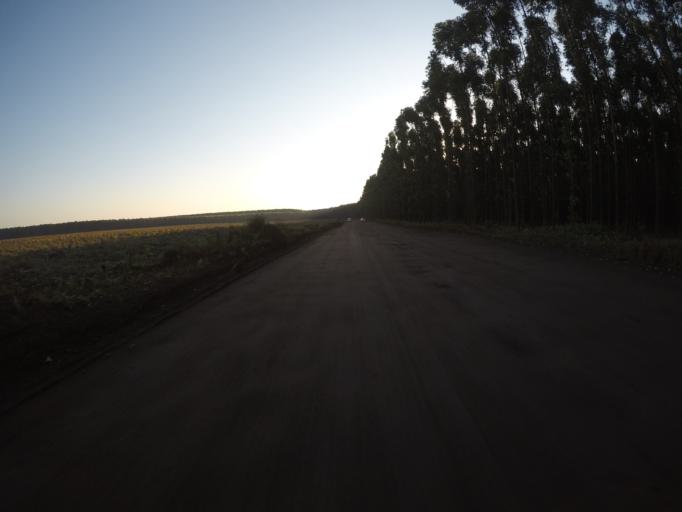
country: ZA
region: KwaZulu-Natal
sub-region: uThungulu District Municipality
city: KwaMbonambi
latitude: -28.6730
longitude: 32.1026
